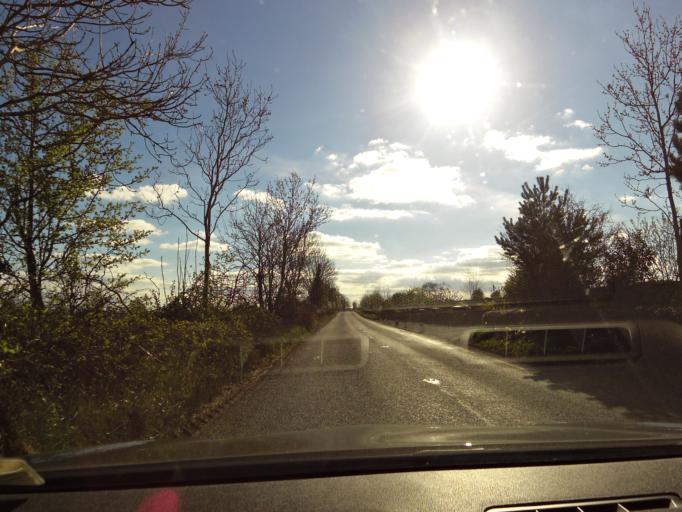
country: IE
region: Connaught
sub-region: County Galway
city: Portumna
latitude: 53.1022
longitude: -8.1428
